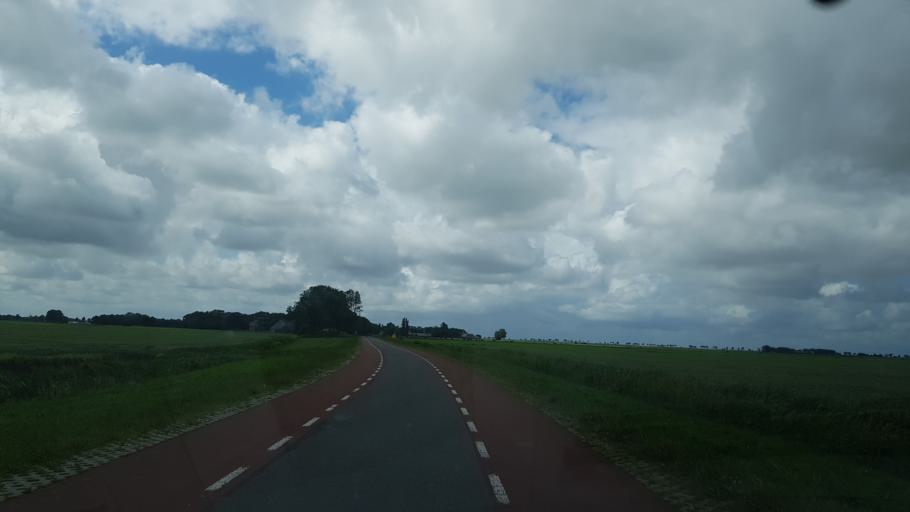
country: NL
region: Groningen
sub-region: Gemeente Winsum
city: Winsum
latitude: 53.3947
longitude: 6.4995
